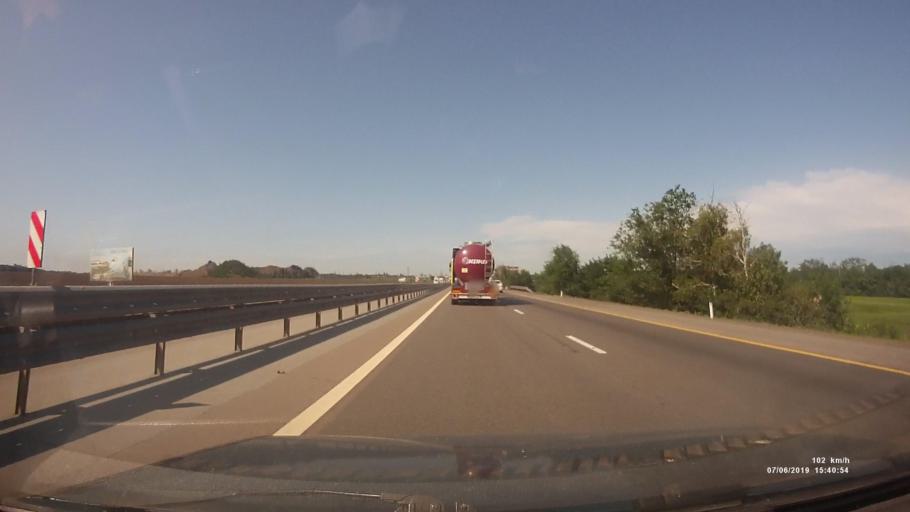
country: RU
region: Rostov
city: Mayskiy
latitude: 47.6857
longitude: 40.0775
